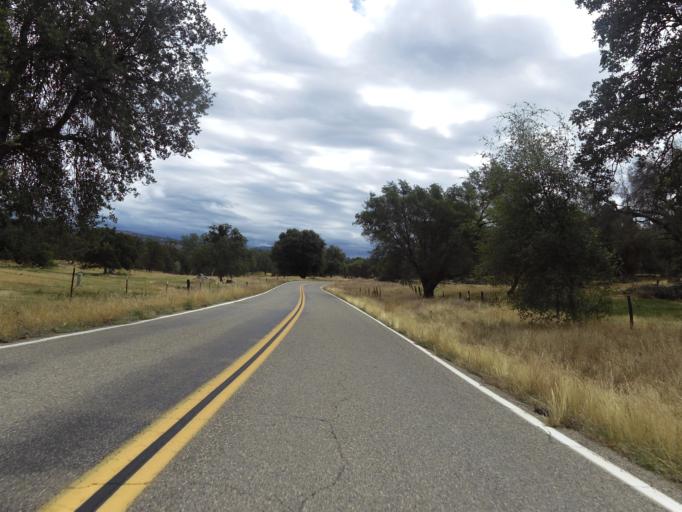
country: US
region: California
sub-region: Madera County
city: Yosemite Lakes
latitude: 37.2438
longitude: -119.8639
